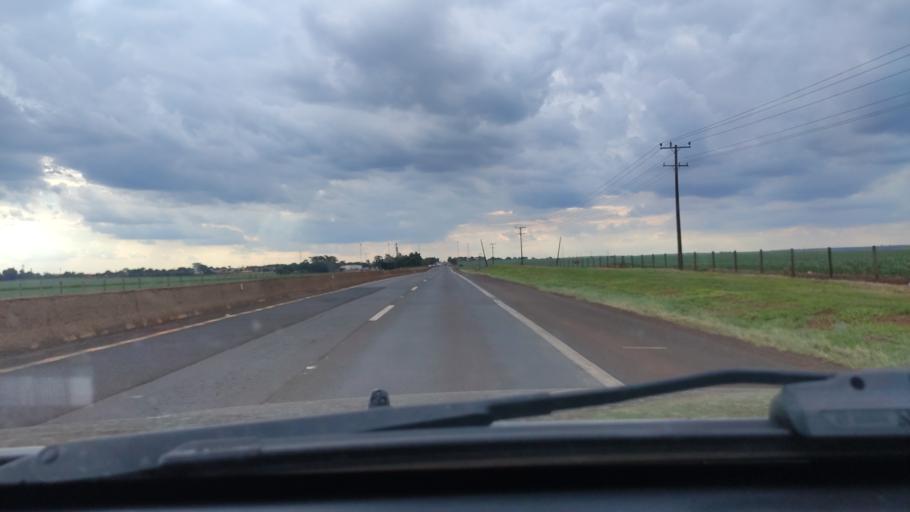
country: BR
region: Sao Paulo
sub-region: Palmital
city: Palmital
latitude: -22.8176
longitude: -50.0496
